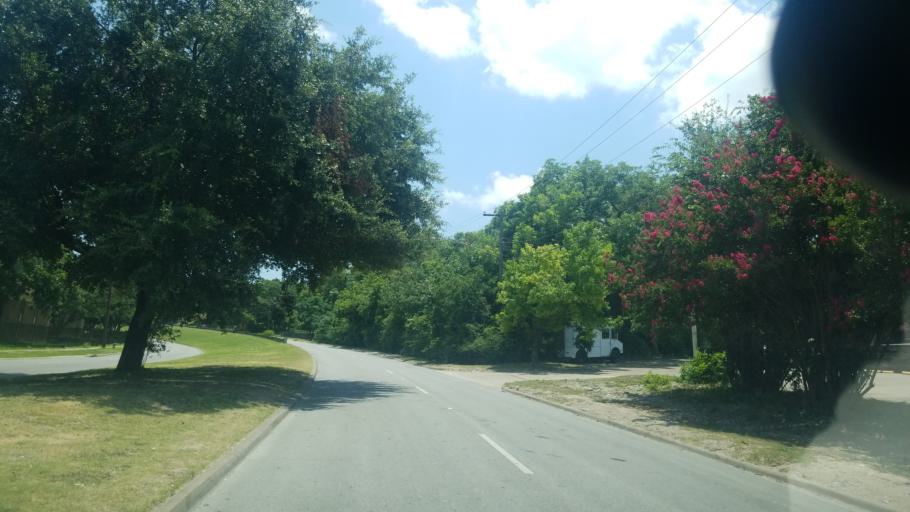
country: US
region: Texas
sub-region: Dallas County
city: Dallas
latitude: 32.7267
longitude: -96.7860
